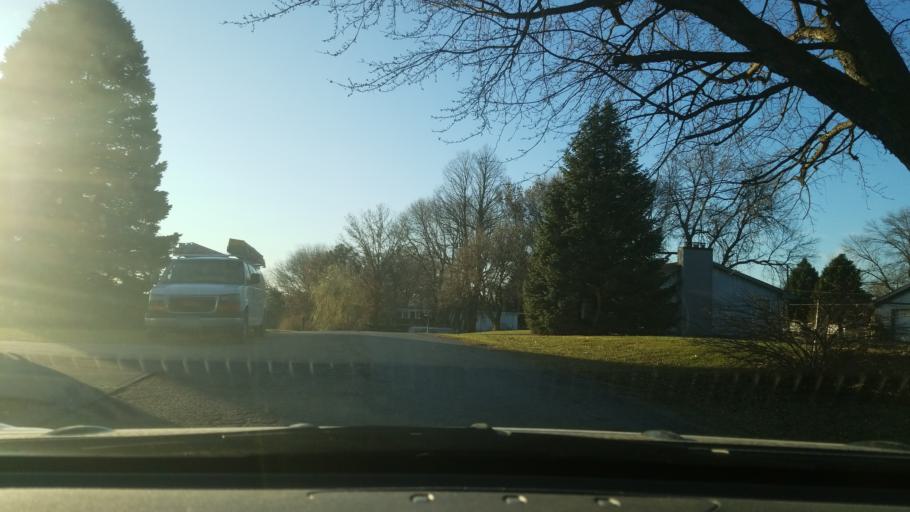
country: US
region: Nebraska
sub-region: Sarpy County
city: La Vista
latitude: 41.1728
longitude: -95.9686
